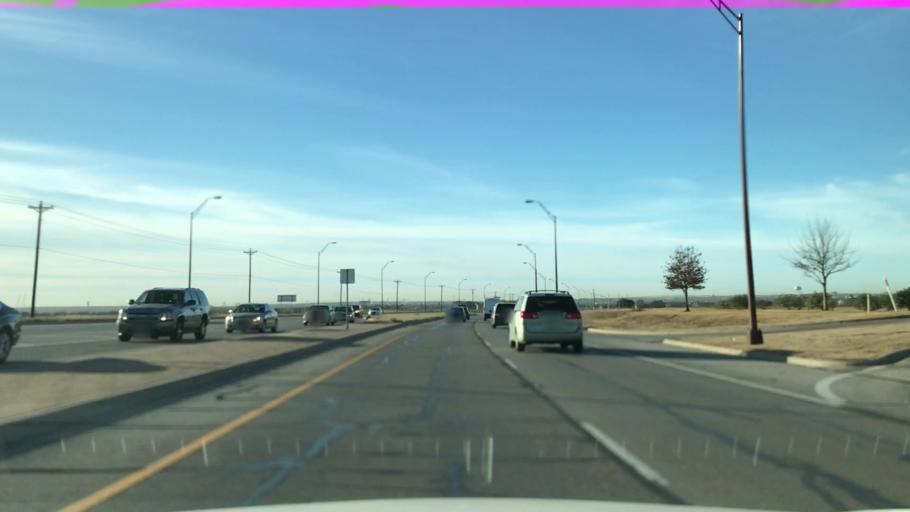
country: US
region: Texas
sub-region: Williamson County
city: Round Rock
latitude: 30.5573
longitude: -97.6457
